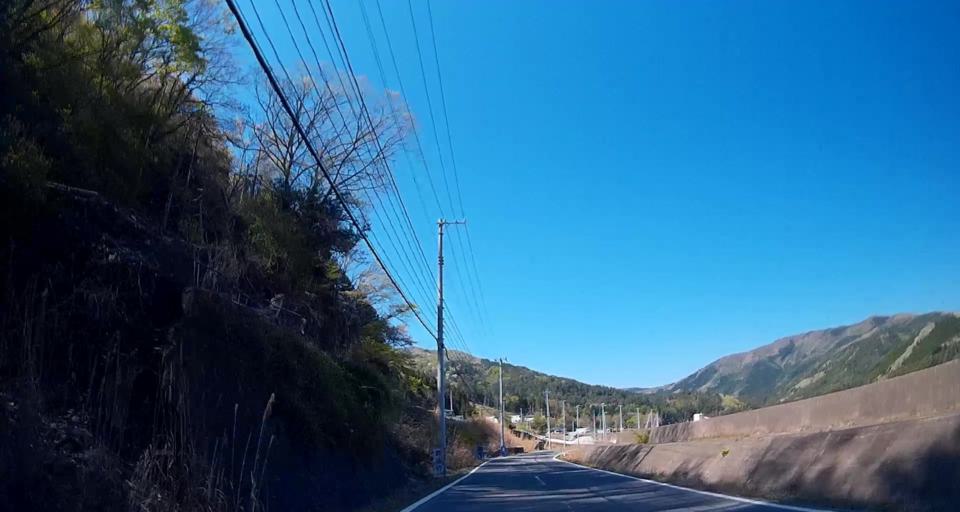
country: JP
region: Miyagi
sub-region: Oshika Gun
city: Onagawa Cho
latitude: 38.5147
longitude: 141.4694
